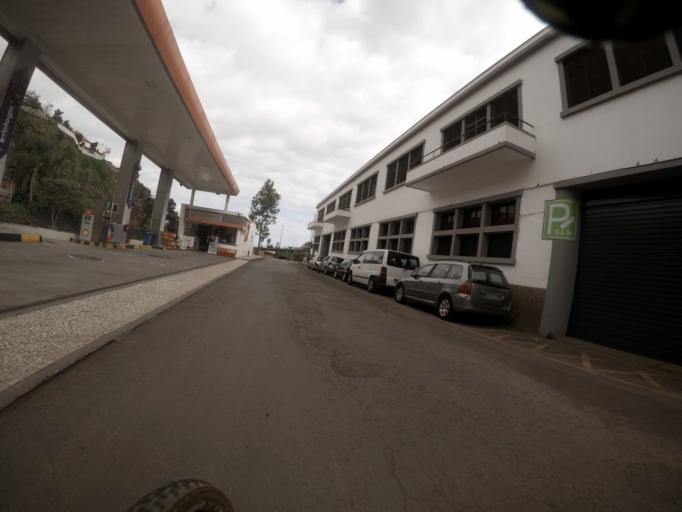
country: PT
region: Madeira
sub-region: Funchal
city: Nossa Senhora do Monte
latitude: 32.6501
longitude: -16.9192
